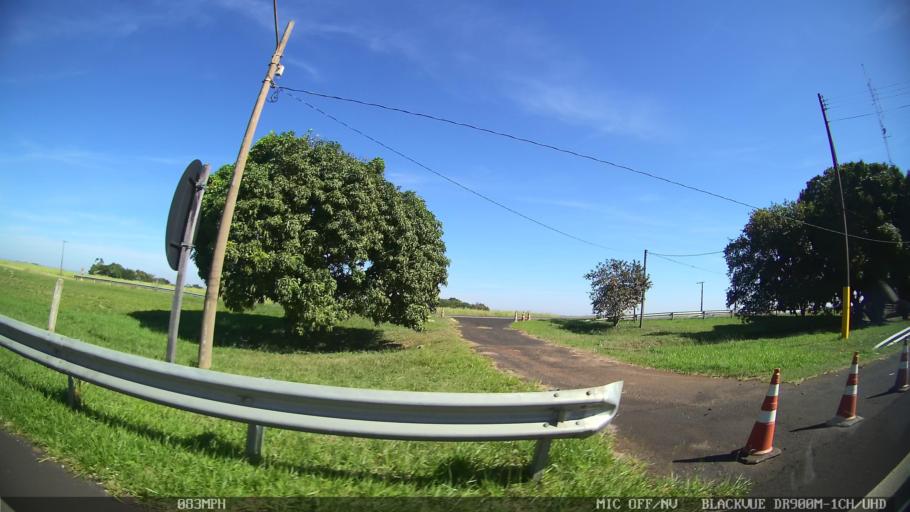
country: BR
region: Sao Paulo
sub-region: Santa Rita Do Passa Quatro
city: Santa Rita do Passa Quatro
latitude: -21.6853
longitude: -47.6014
